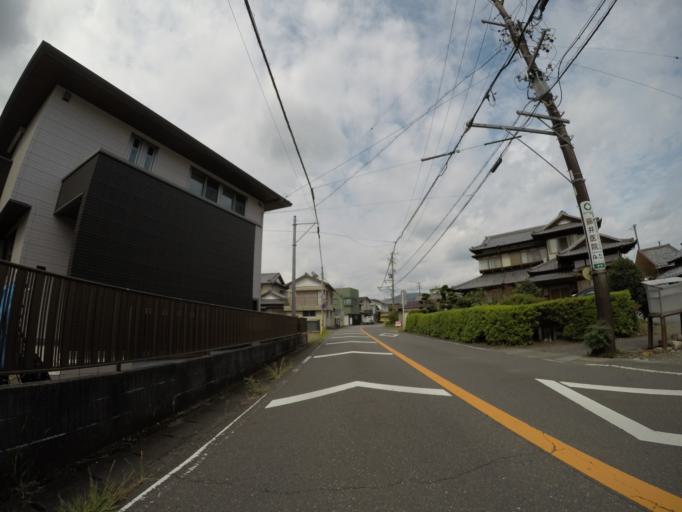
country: JP
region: Shizuoka
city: Shimada
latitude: 34.8516
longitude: 138.1829
